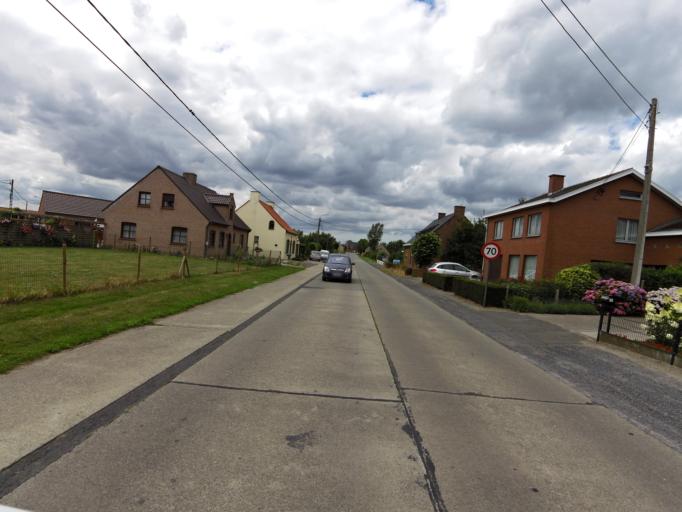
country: BE
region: Flanders
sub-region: Provincie West-Vlaanderen
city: Kortemark
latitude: 51.0393
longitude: 3.0327
